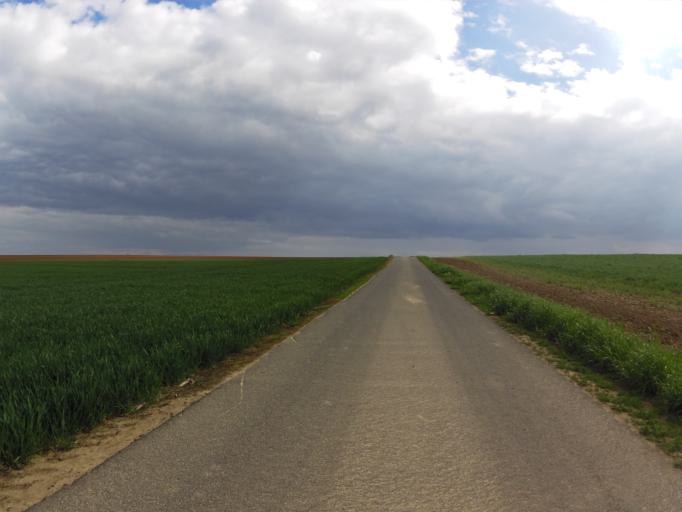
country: DE
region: Bavaria
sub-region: Regierungsbezirk Unterfranken
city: Oberpleichfeld
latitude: 49.8606
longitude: 10.0823
